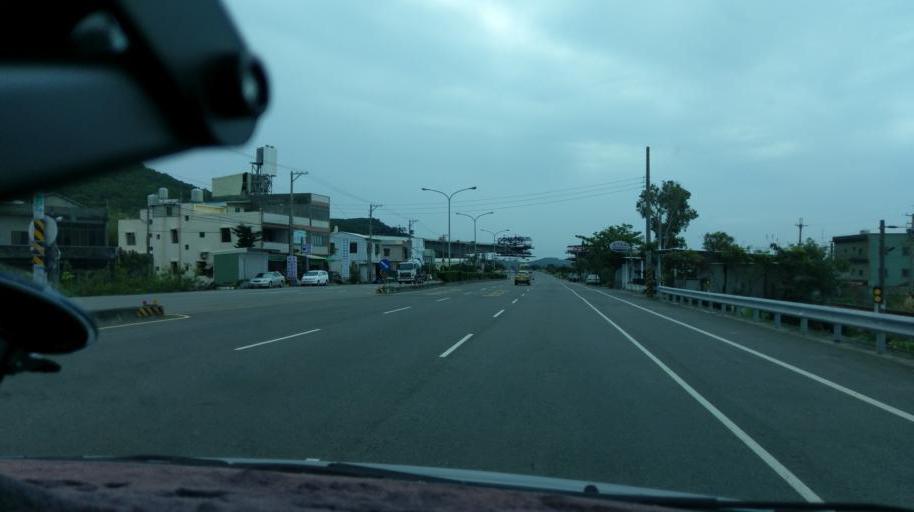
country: TW
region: Taiwan
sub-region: Miaoli
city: Miaoli
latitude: 24.5337
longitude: 120.6940
